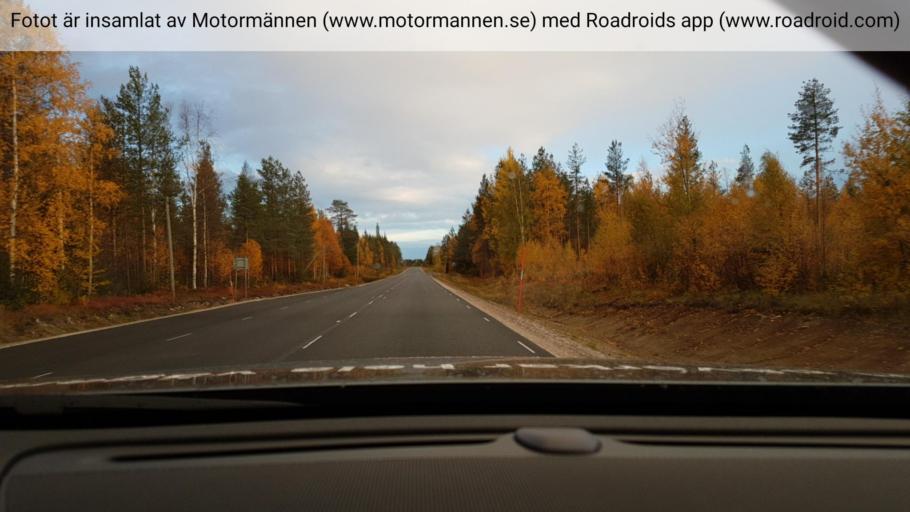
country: SE
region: Norrbotten
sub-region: Overkalix Kommun
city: OEverkalix
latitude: 66.3823
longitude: 22.8304
